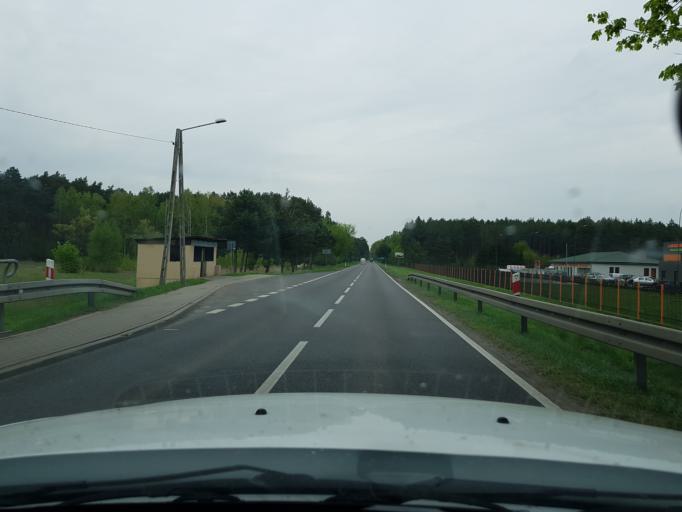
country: PL
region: West Pomeranian Voivodeship
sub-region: Powiat mysliborski
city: Debno
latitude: 52.6958
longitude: 14.6897
